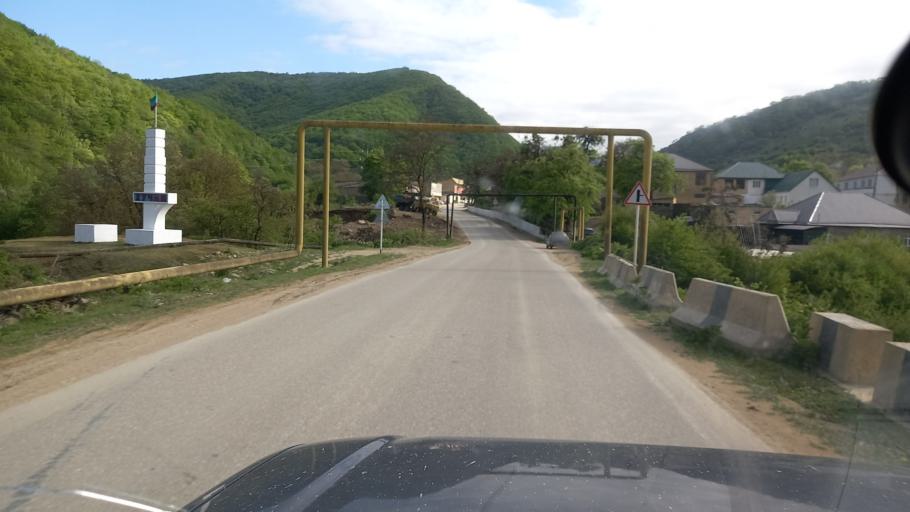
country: RU
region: Dagestan
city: Khuchni
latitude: 41.9635
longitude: 47.9575
